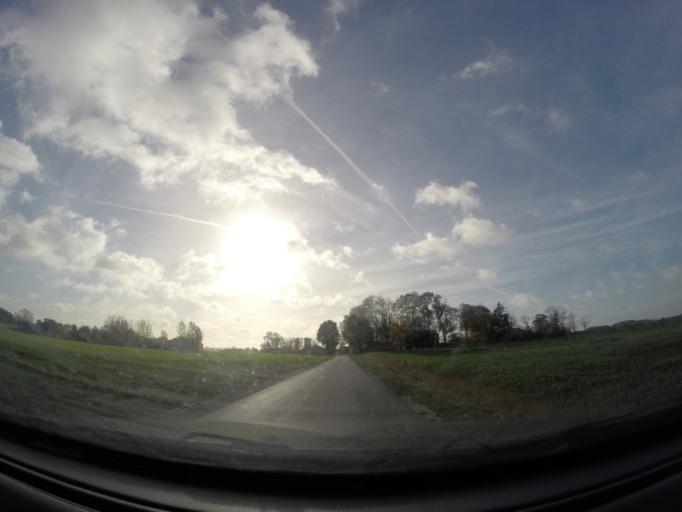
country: DK
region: South Denmark
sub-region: Faaborg-Midtfyn Kommune
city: Ringe
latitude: 55.2075
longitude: 10.5607
